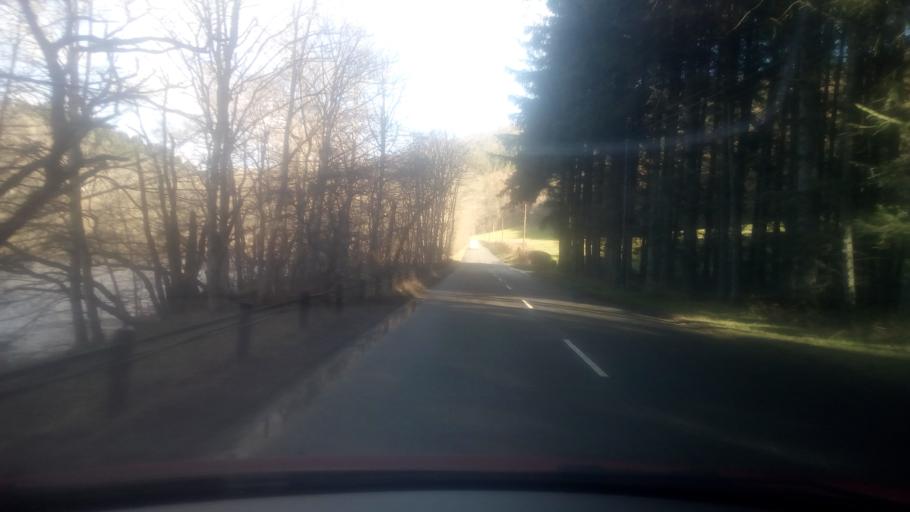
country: GB
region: Scotland
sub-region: The Scottish Borders
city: Selkirk
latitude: 55.5931
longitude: -2.8669
